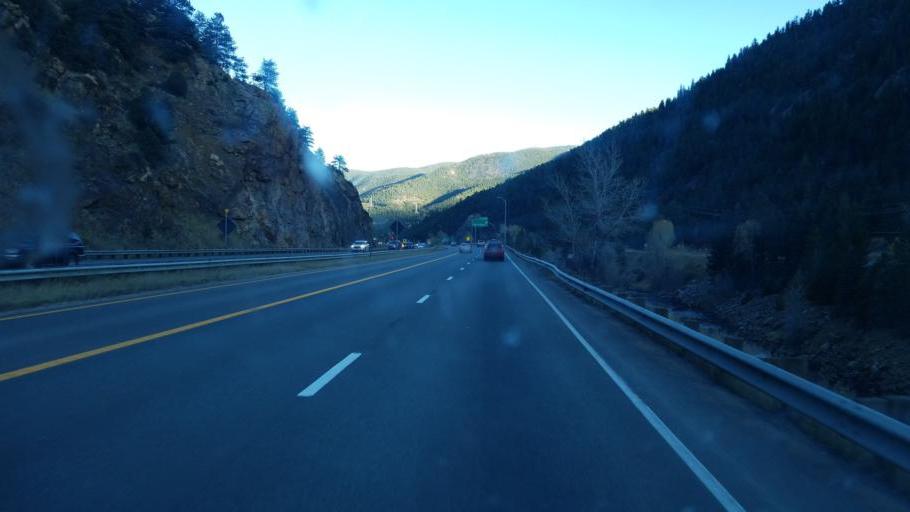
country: US
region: Colorado
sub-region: Clear Creek County
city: Idaho Springs
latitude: 39.7457
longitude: -105.5402
